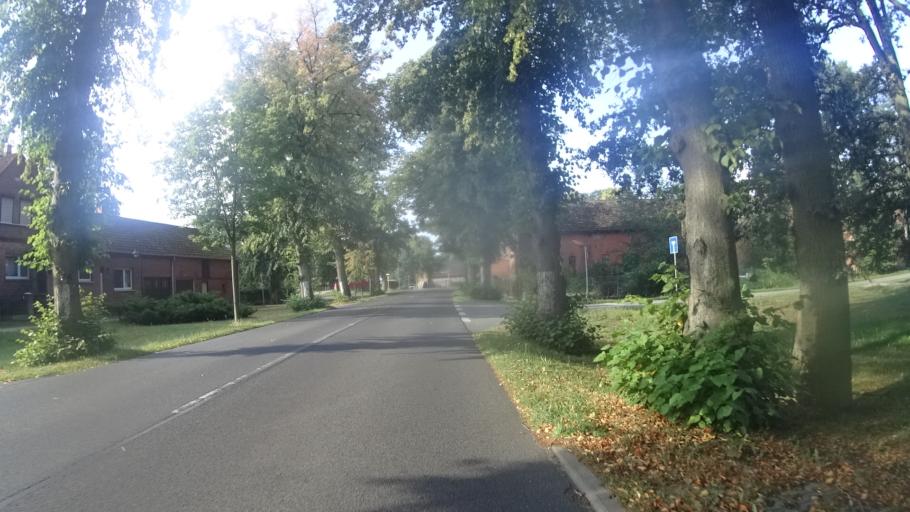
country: DE
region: Brandenburg
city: Cumlosen
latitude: 53.0330
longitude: 11.6598
